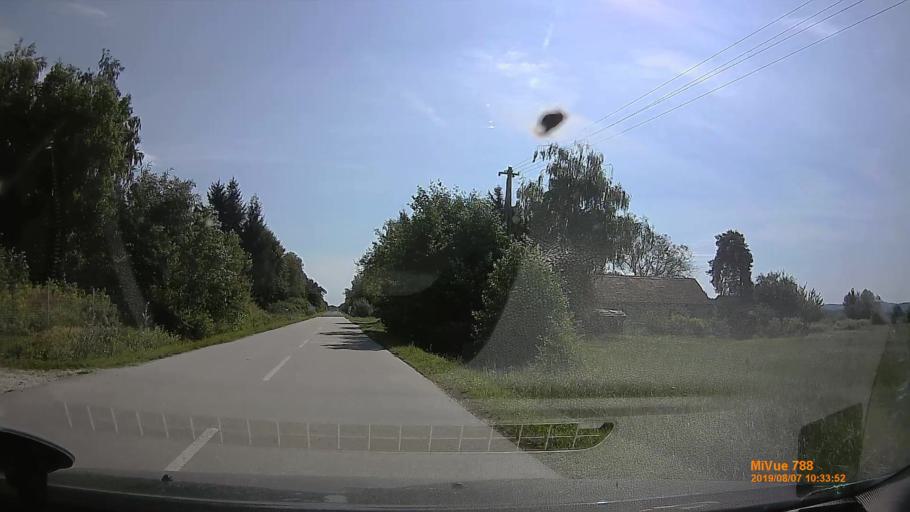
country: SI
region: Lendava-Lendva
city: Lendava
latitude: 46.6168
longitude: 16.4190
